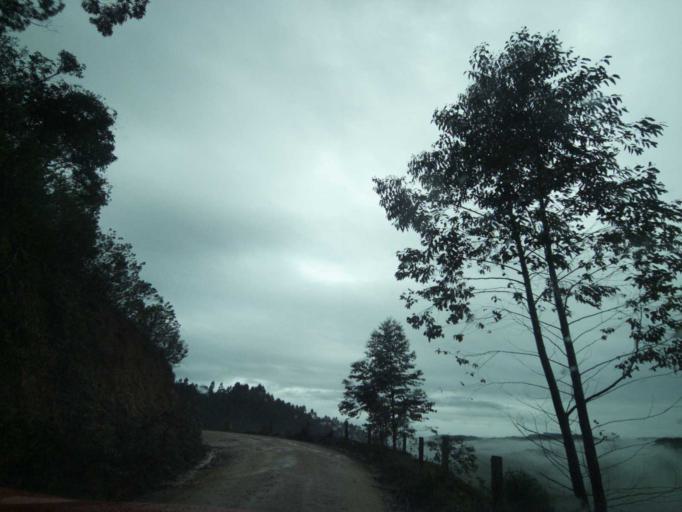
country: BR
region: Santa Catarina
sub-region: Anitapolis
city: Anitapolis
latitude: -27.9266
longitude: -49.1823
